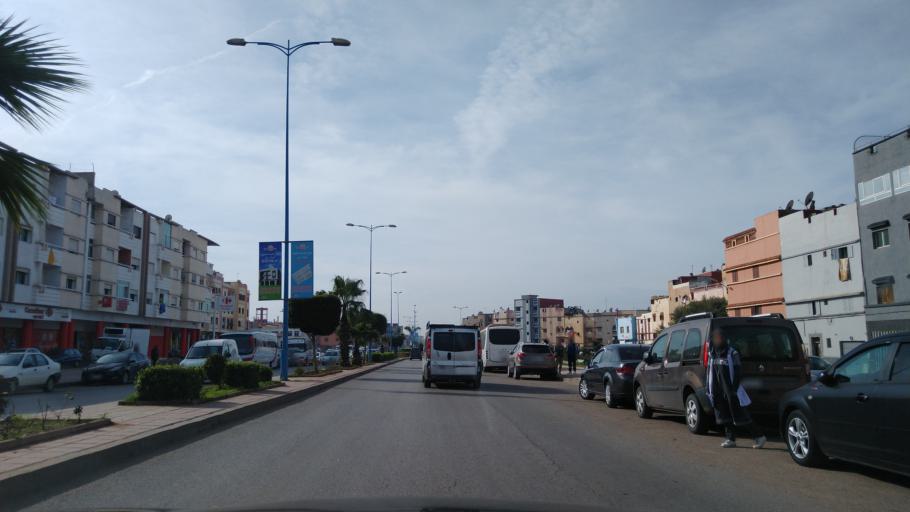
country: MA
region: Grand Casablanca
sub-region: Mohammedia
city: Mohammedia
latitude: 33.6865
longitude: -7.3780
